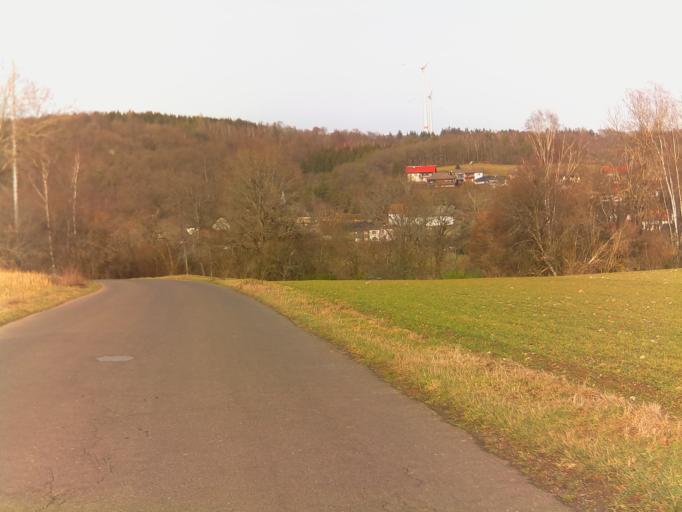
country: DE
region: Rheinland-Pfalz
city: Ellweiler
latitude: 49.6098
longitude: 7.1467
